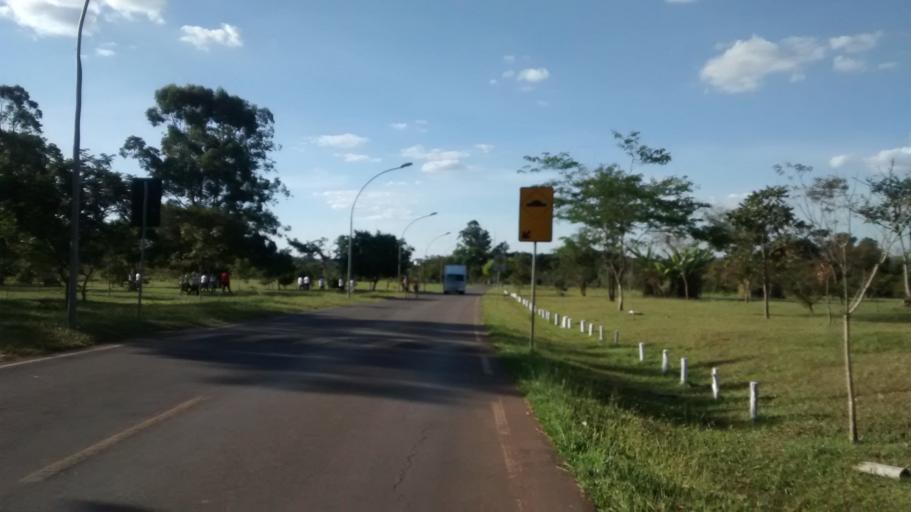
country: BR
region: Federal District
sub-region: Brasilia
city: Brasilia
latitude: -15.8355
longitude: -48.0246
